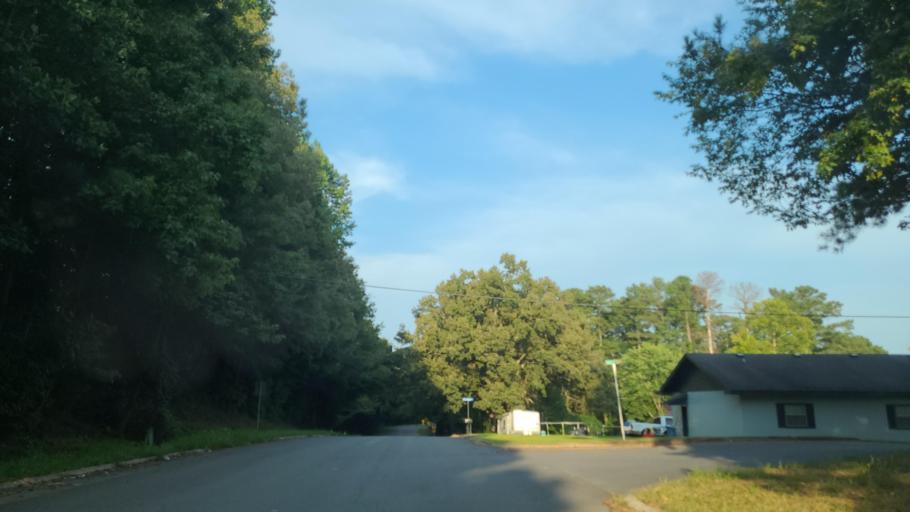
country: US
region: Georgia
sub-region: Whitfield County
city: Dalton
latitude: 34.6883
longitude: -84.9843
